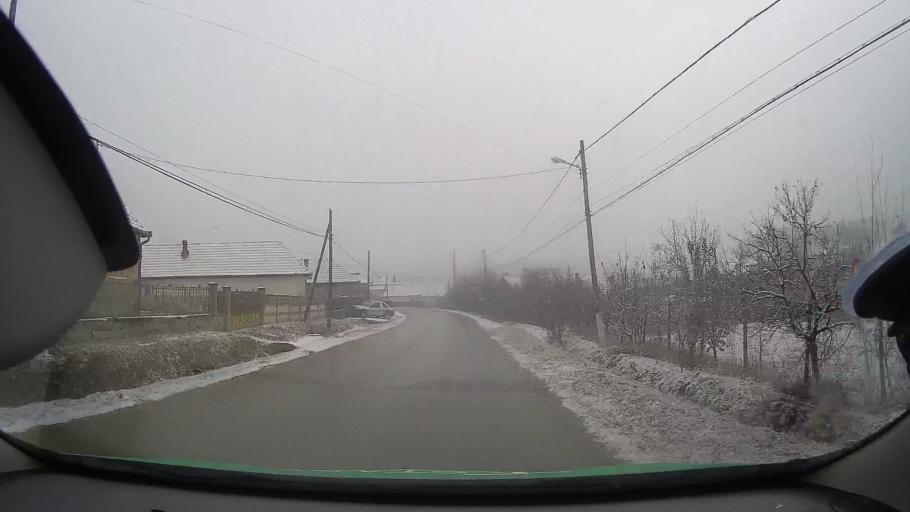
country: RO
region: Alba
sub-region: Comuna Lopadea Noua
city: Lopadea Noua
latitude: 46.2900
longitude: 23.8247
